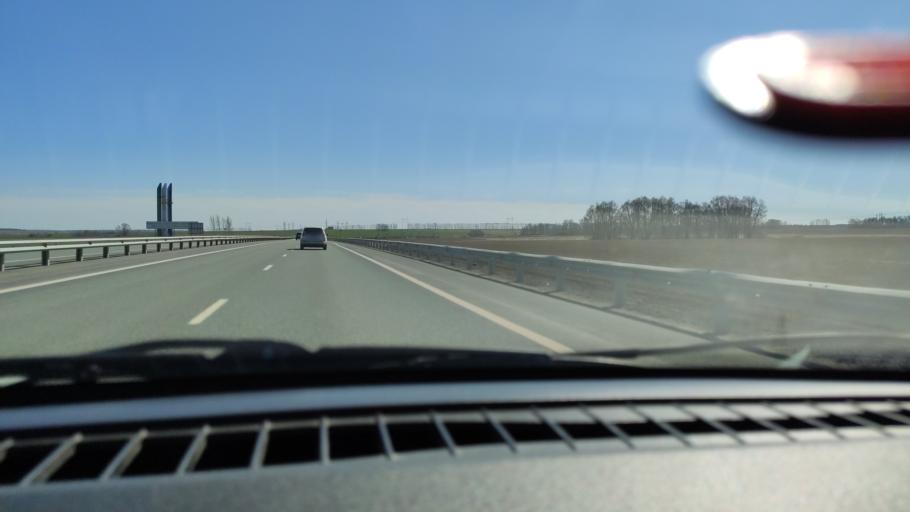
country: RU
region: Bashkortostan
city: Tolbazy
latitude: 54.2691
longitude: 55.8811
